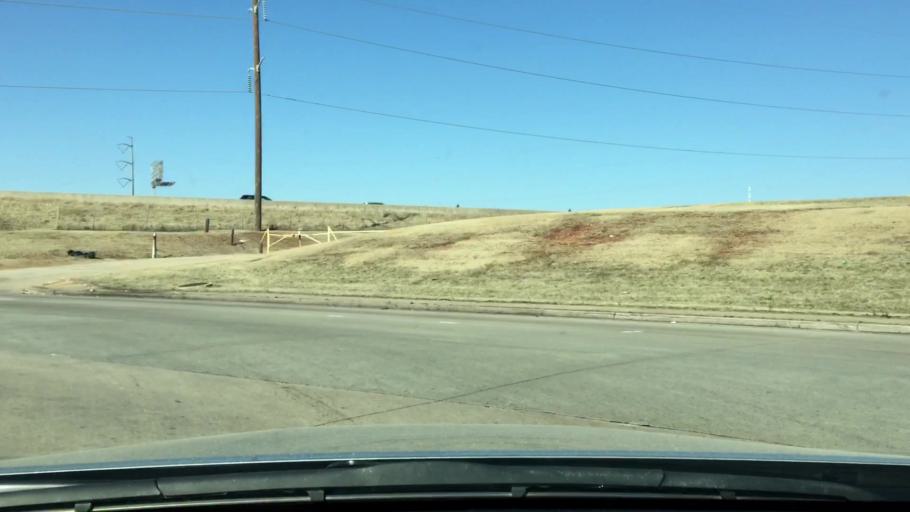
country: US
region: Oklahoma
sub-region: Oklahoma County
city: The Village
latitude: 35.5945
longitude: -97.5063
